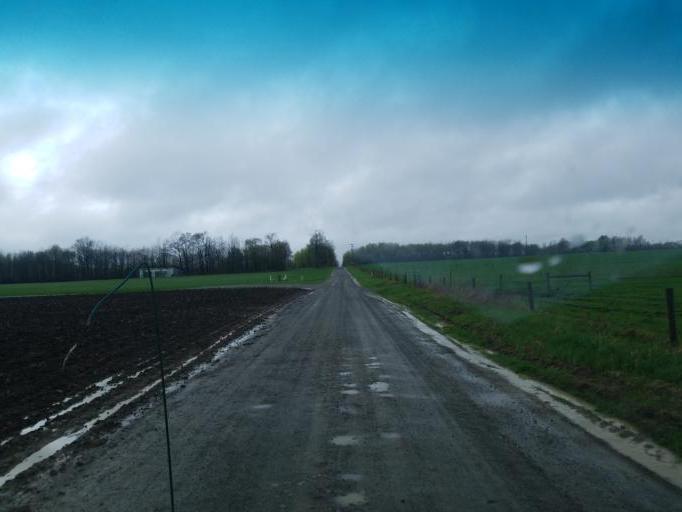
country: US
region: Pennsylvania
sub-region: Tioga County
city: Westfield
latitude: 41.9799
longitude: -77.7057
